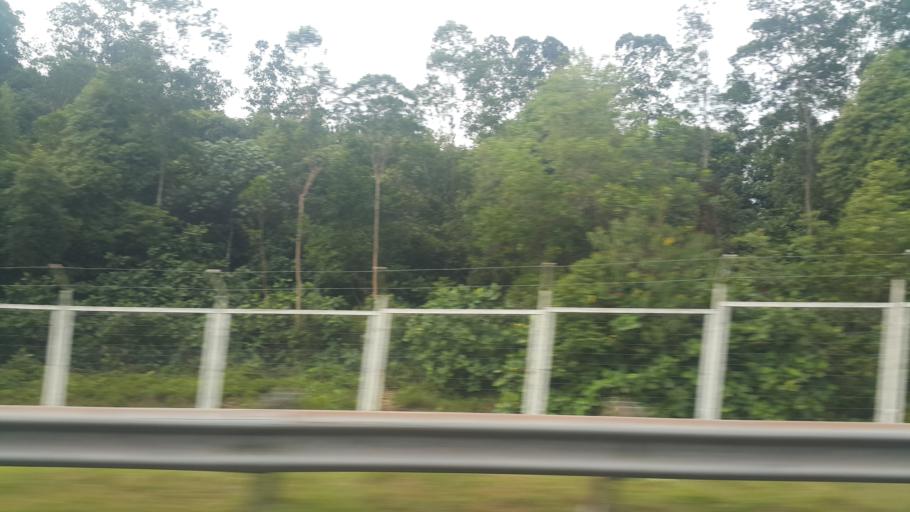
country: MY
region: Johor
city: Pekan Nenas
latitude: 1.3749
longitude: 103.6063
